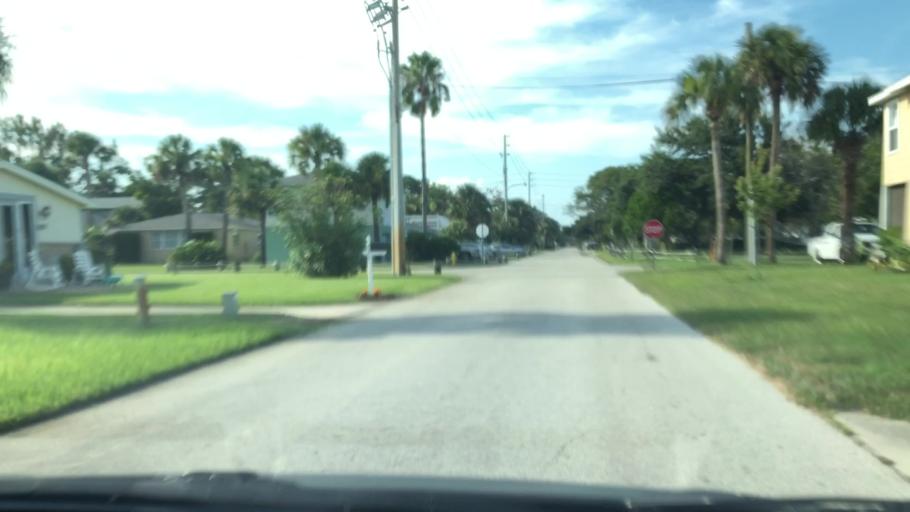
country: US
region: Florida
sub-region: Duval County
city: Jacksonville Beach
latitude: 30.2949
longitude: -81.3955
